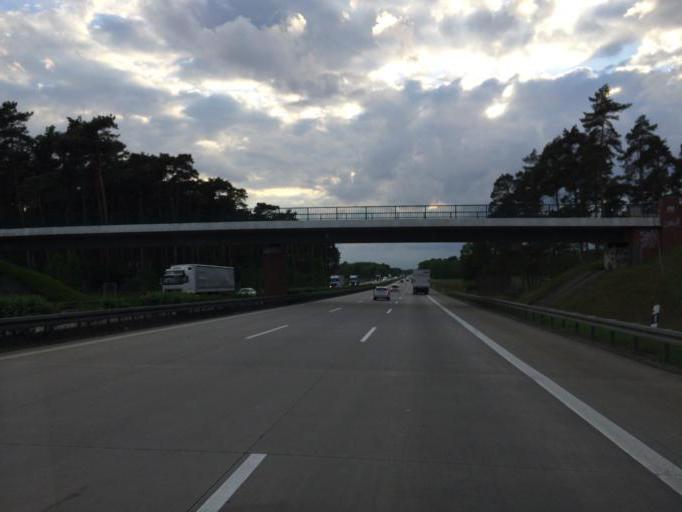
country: DE
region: Saxony-Anhalt
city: Mockern
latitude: 52.2345
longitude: 12.0138
